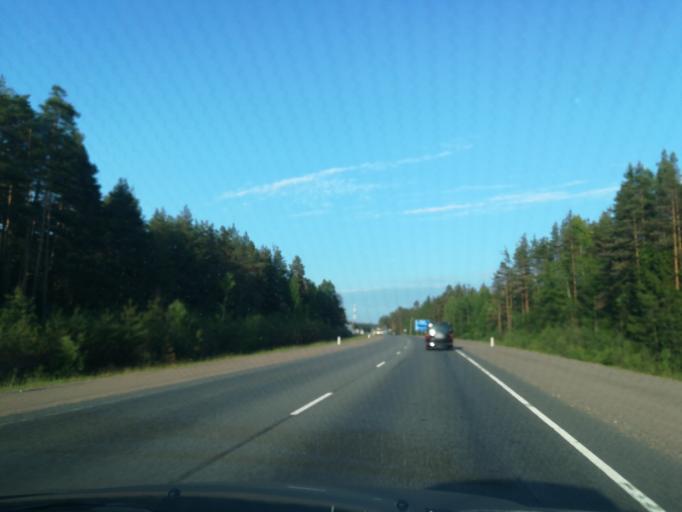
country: RU
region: Leningrad
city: Vyborg
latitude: 60.6690
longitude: 28.8918
